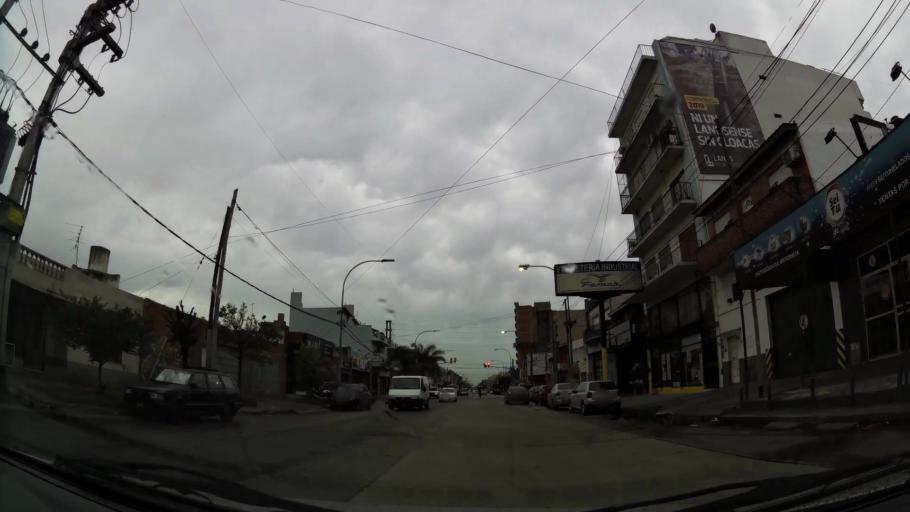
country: AR
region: Buenos Aires
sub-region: Partido de Lanus
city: Lanus
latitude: -34.6938
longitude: -58.4060
